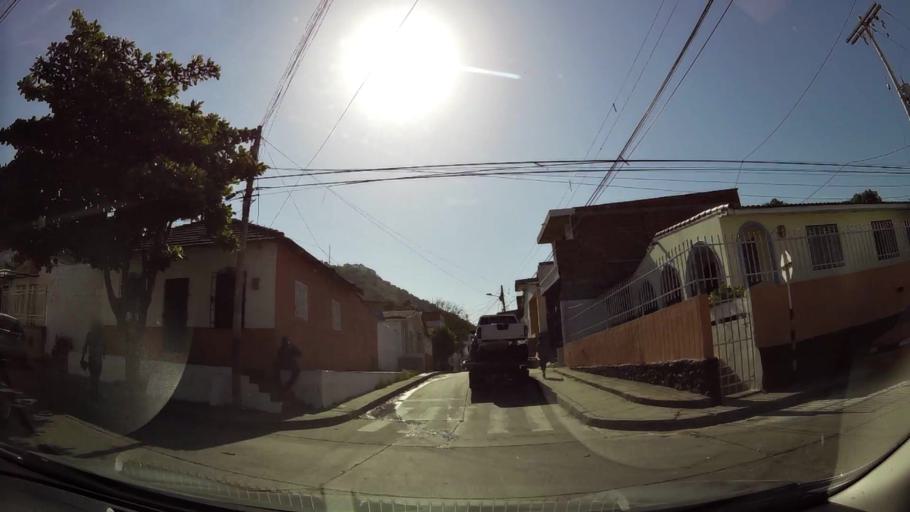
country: CO
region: Bolivar
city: Cartagena
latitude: 10.4218
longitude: -75.5307
